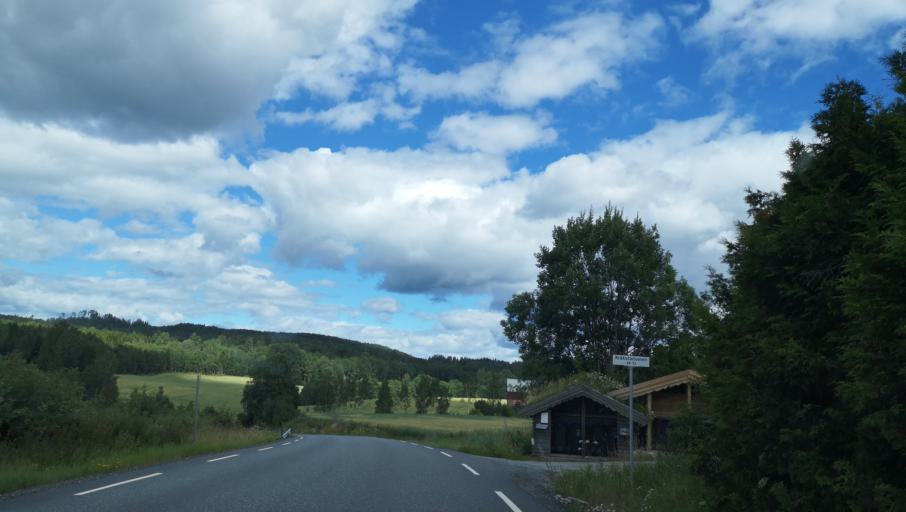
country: NO
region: Ostfold
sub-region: Hobol
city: Tomter
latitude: 59.6700
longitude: 11.0053
